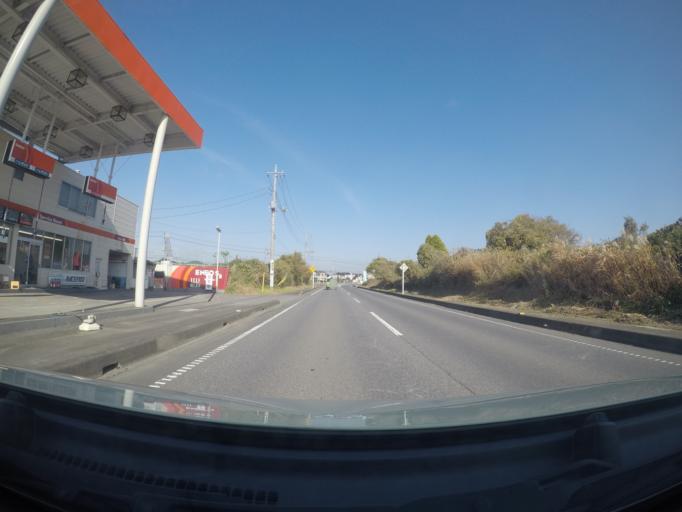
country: JP
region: Ibaraki
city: Makabe
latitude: 36.2469
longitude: 140.0693
